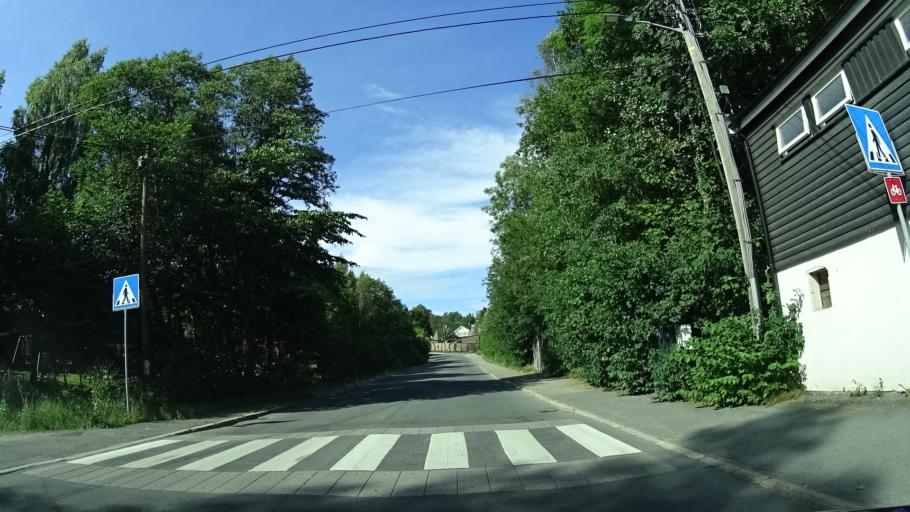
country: NO
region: Oslo
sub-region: Oslo
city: Sjolyststranda
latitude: 59.9573
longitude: 10.6898
